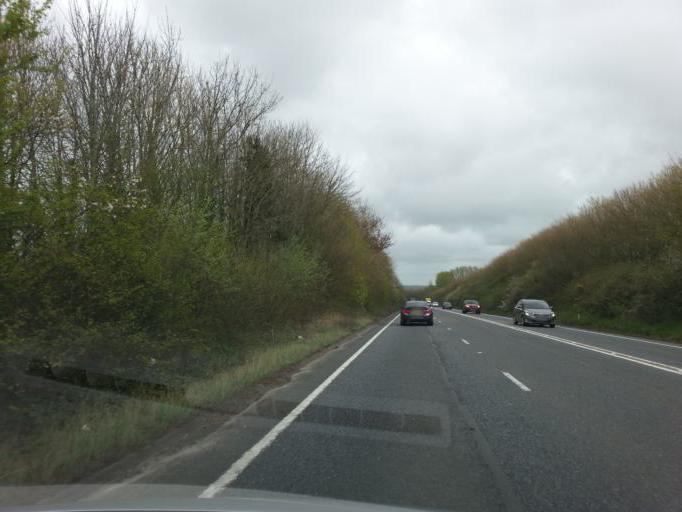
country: GB
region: England
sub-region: Somerset
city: South Petherton
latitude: 50.9393
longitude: -2.8215
